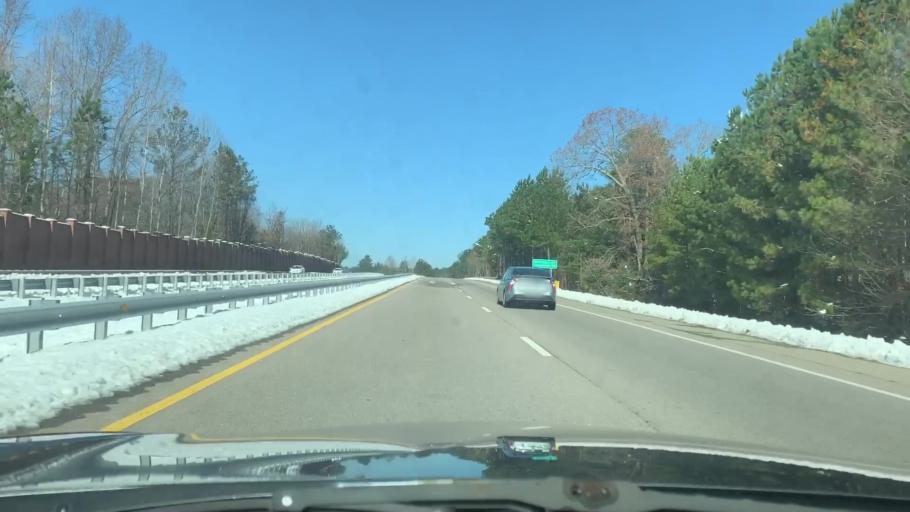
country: US
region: North Carolina
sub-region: Durham County
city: Durham
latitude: 36.0268
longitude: -78.9605
